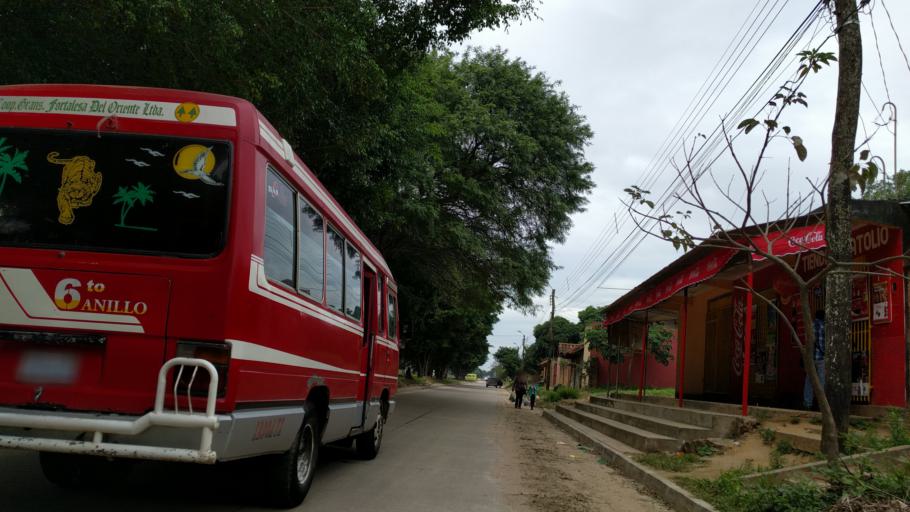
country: BO
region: Santa Cruz
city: Santa Cruz de la Sierra
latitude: -17.8157
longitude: -63.2278
